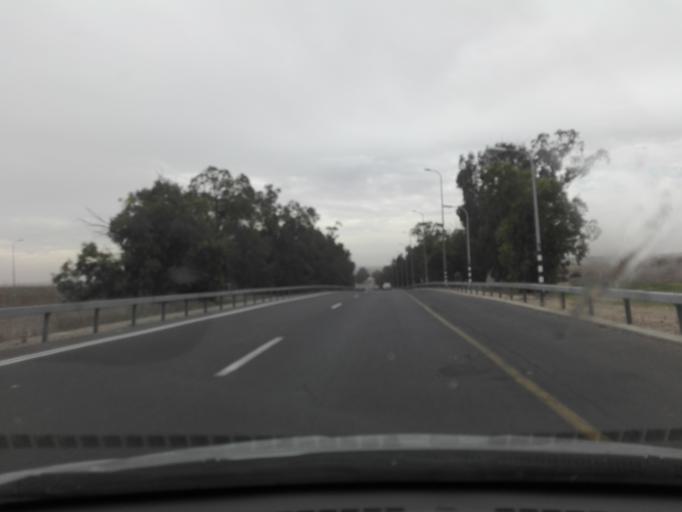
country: IL
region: Southern District
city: Qiryat Gat
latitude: 31.4988
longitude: 34.7826
